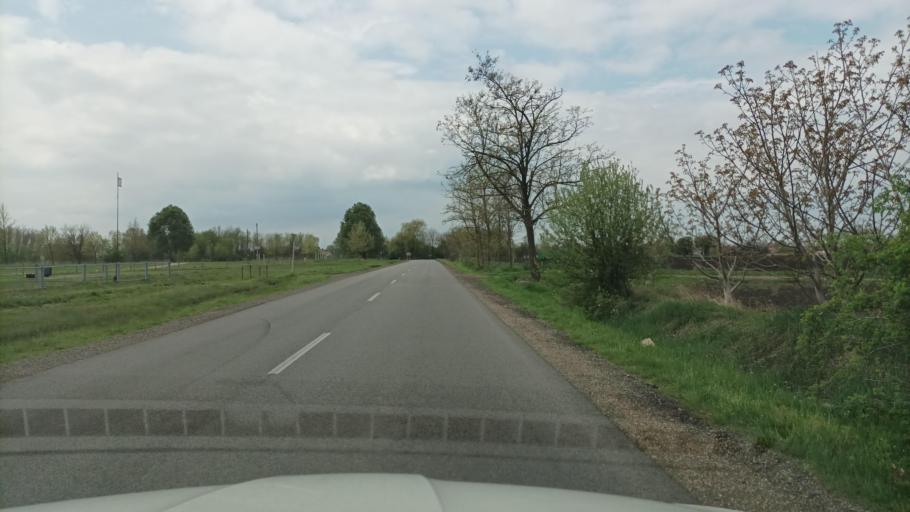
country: HU
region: Pest
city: Nagykoros
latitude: 47.0296
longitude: 19.8113
